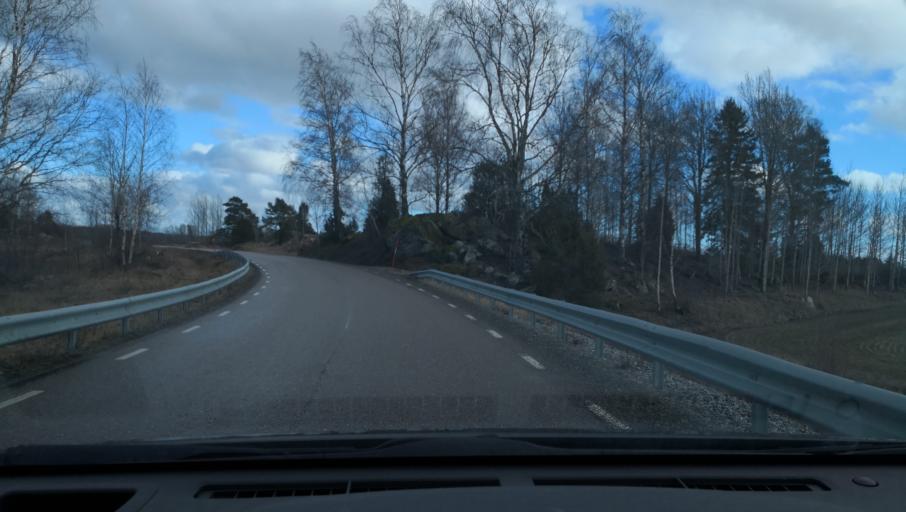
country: SE
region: OErebro
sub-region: Lindesbergs Kommun
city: Fellingsbro
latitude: 59.3499
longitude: 15.6789
